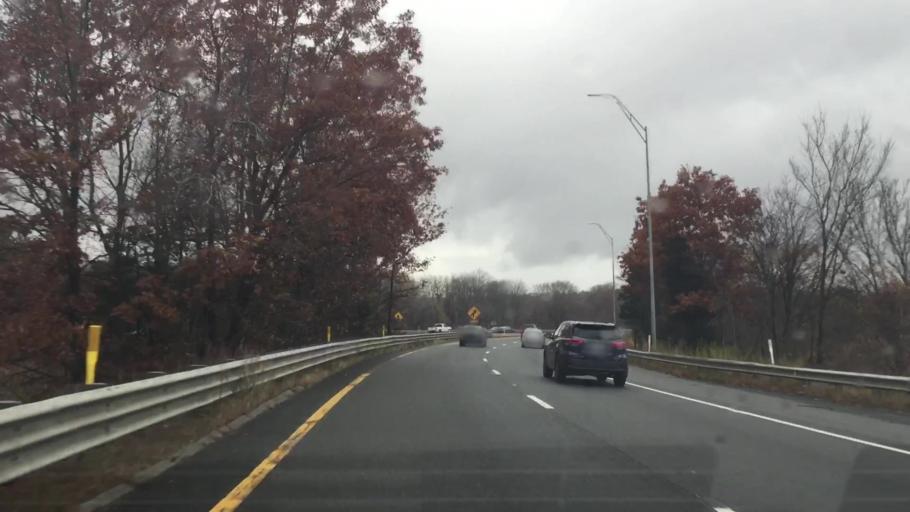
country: US
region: Massachusetts
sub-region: Essex County
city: Amesbury
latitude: 42.8619
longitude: -70.8925
